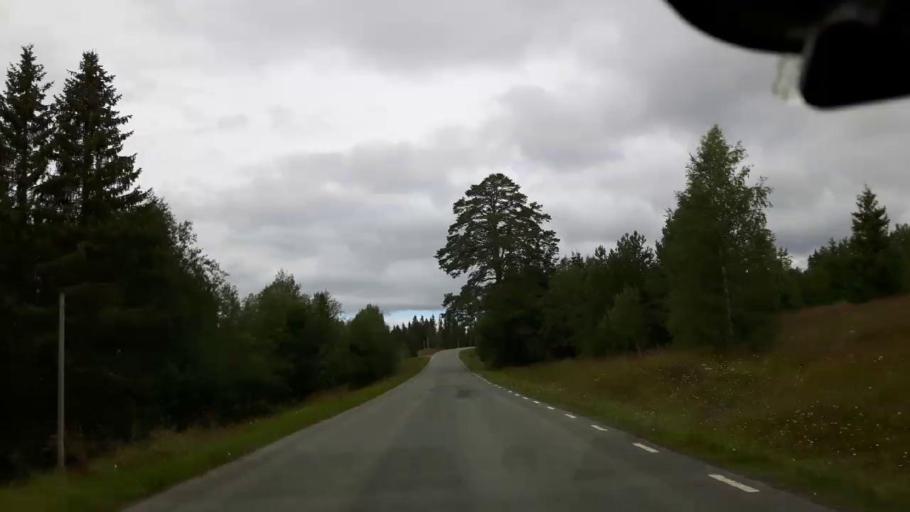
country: SE
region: Jaemtland
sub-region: Krokoms Kommun
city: Valla
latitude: 63.5119
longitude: 13.8835
